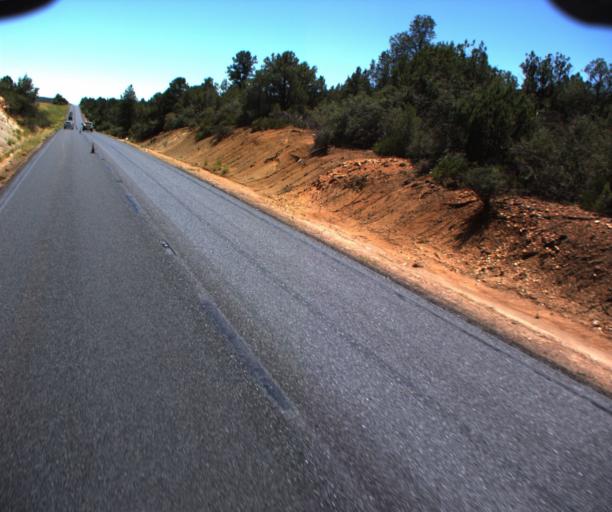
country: US
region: Arizona
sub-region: Gila County
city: Payson
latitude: 34.2115
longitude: -111.3319
